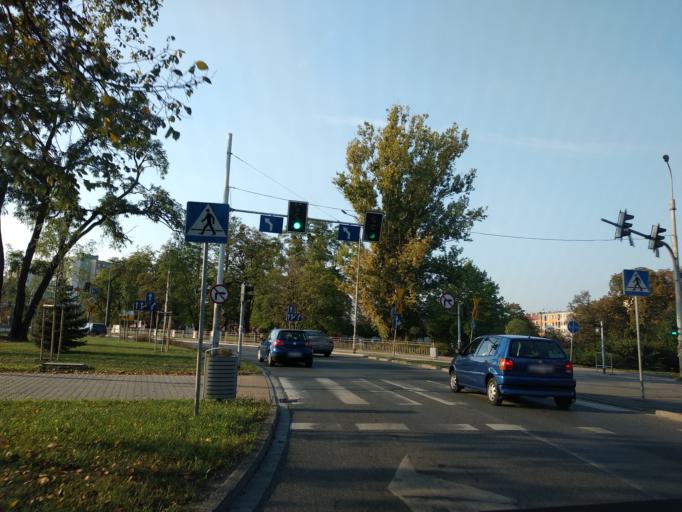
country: PL
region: Lower Silesian Voivodeship
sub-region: Powiat wroclawski
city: Wroclaw
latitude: 51.0849
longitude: 17.0488
